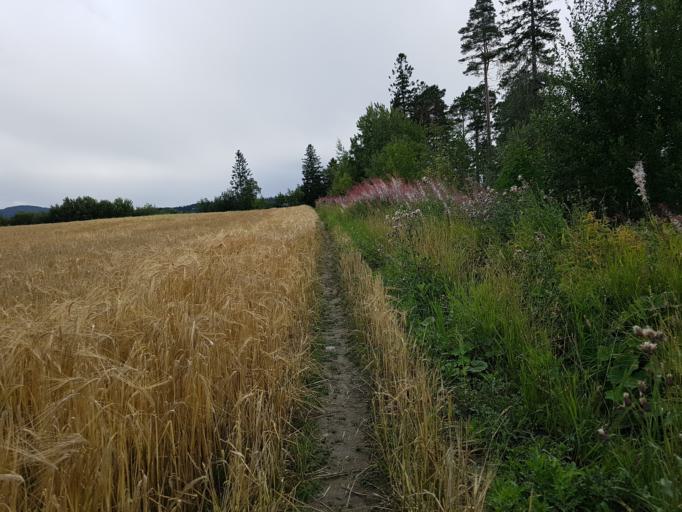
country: NO
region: Sor-Trondelag
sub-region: Trondheim
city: Trondheim
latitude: 63.4233
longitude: 10.4784
